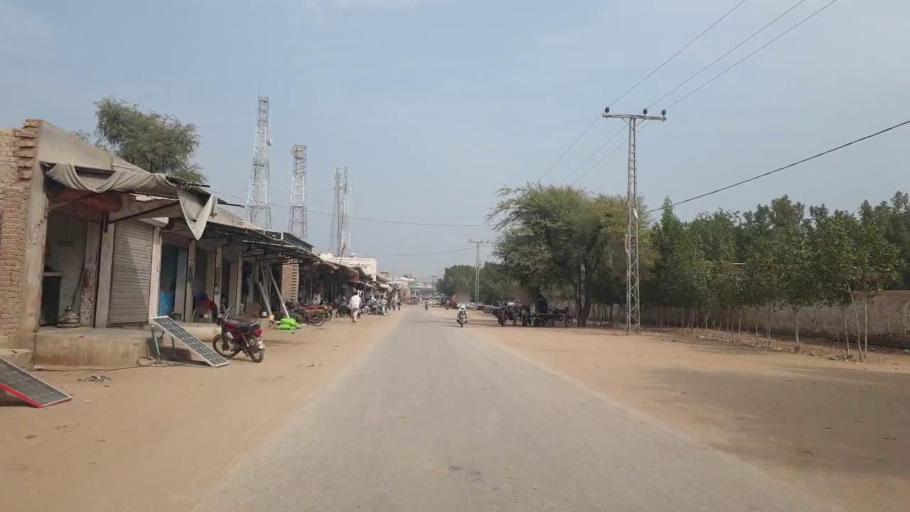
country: PK
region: Sindh
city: Sann
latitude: 26.0386
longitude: 68.1358
